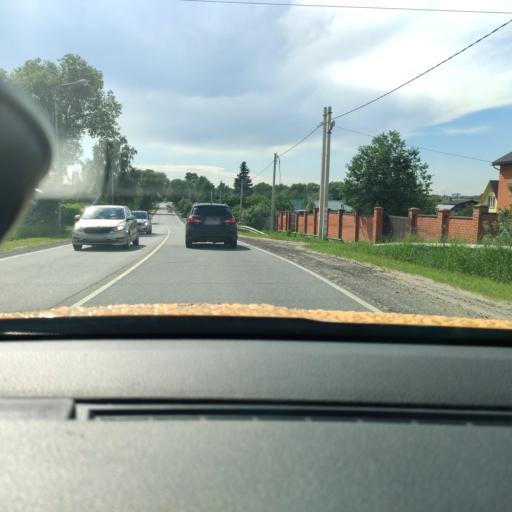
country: RU
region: Moskovskaya
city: Stupino
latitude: 54.9446
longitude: 38.0275
